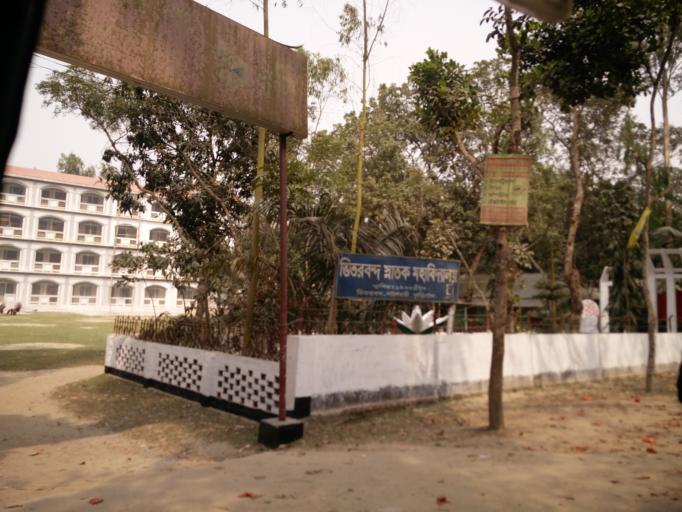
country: BD
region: Rangpur Division
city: Nageswari
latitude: 25.8855
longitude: 89.7007
